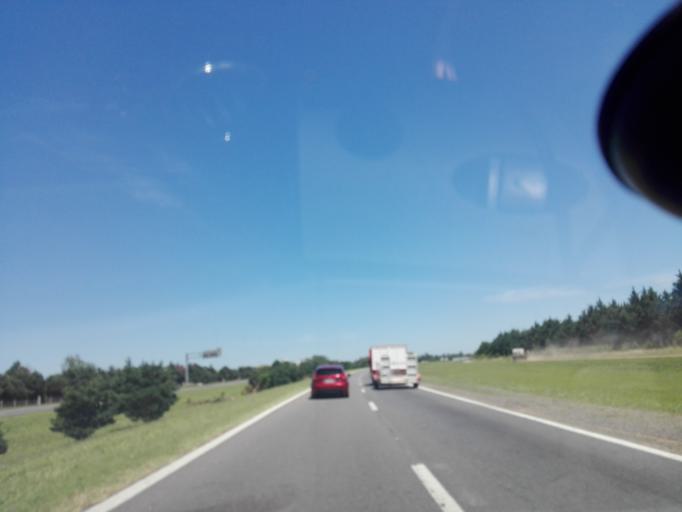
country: AR
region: Santa Fe
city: Funes
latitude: -32.9386
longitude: -60.8251
